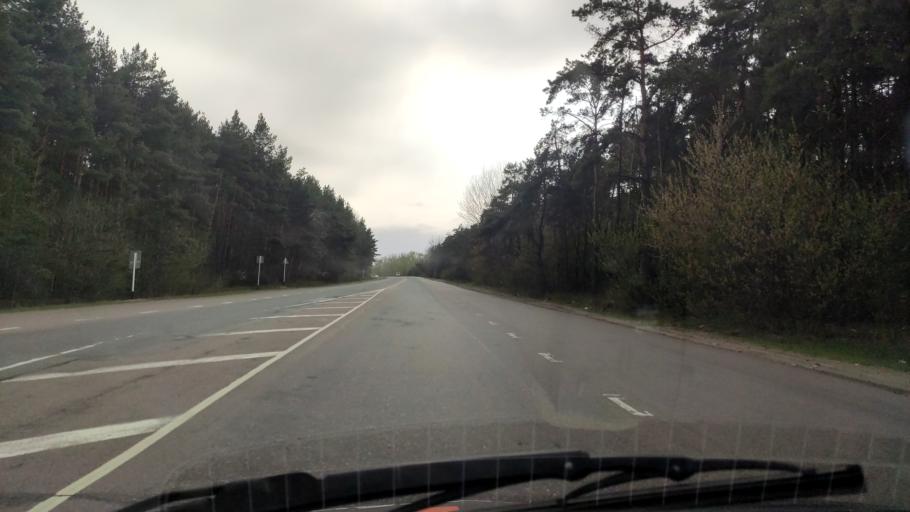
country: RU
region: Kursk
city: Gorshechnoye
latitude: 51.4671
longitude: 37.9319
